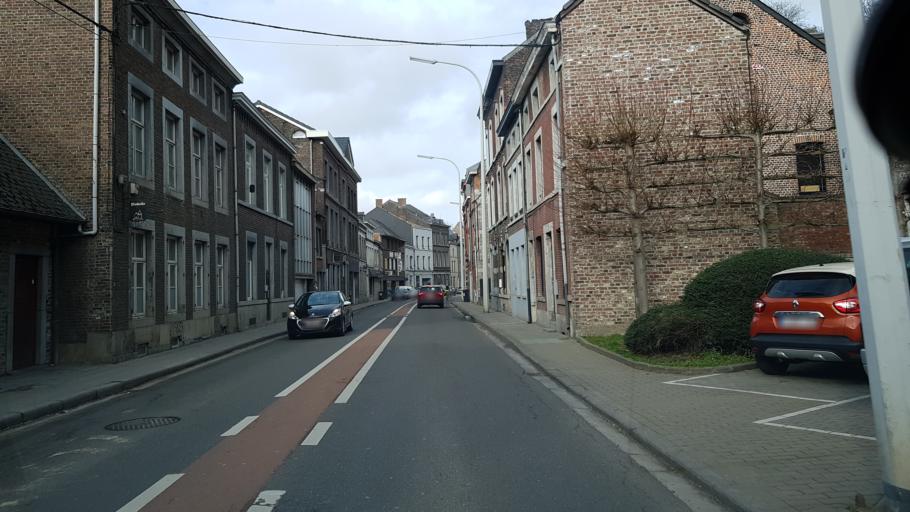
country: BE
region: Wallonia
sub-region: Province de Liege
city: Huy
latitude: 50.5293
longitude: 5.2212
